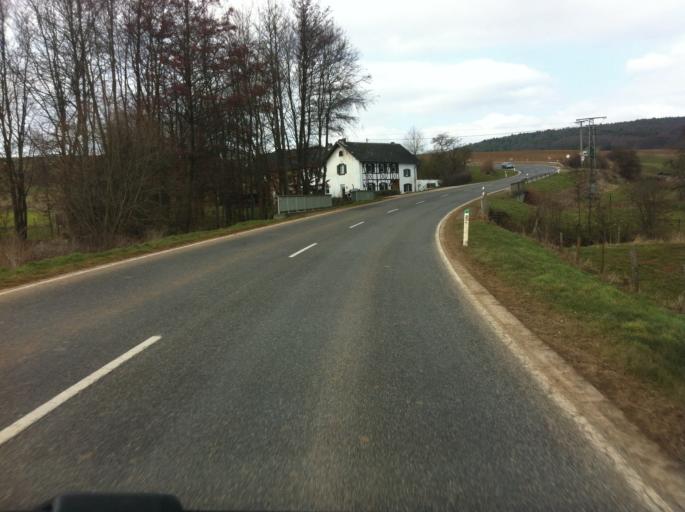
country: DE
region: North Rhine-Westphalia
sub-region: Regierungsbezirk Koln
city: Bad Munstereifel
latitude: 50.5539
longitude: 6.7201
